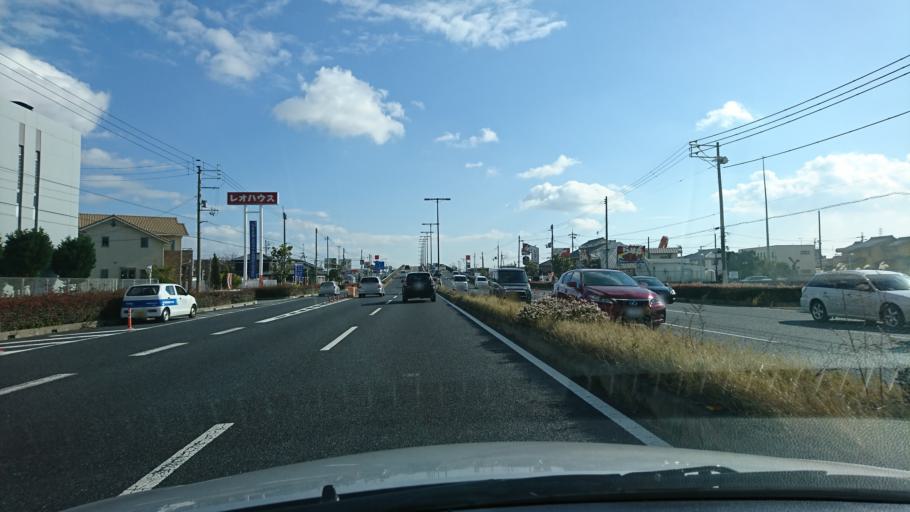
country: JP
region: Hyogo
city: Kakogawacho-honmachi
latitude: 34.7577
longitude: 134.8212
